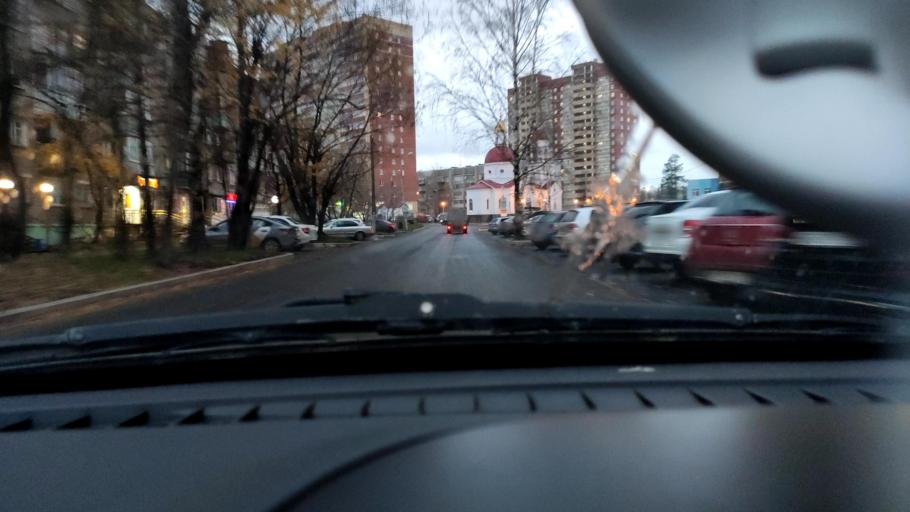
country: RU
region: Perm
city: Kondratovo
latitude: 58.0494
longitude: 56.0886
